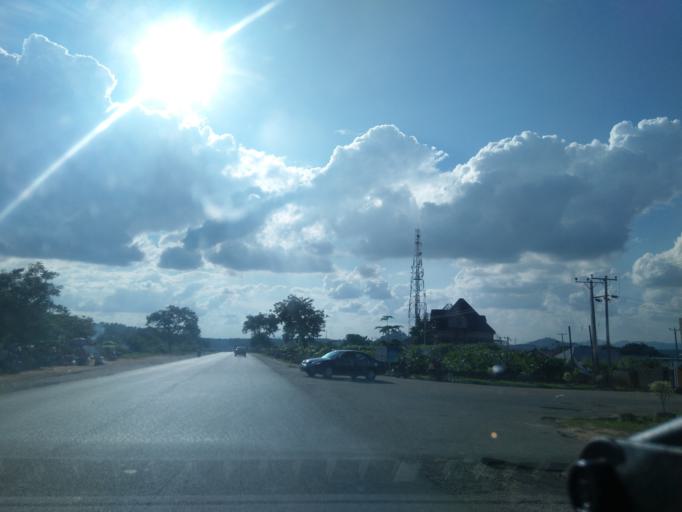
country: NG
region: Abuja Federal Capital Territory
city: Abuja
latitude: 9.0425
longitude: 7.3913
